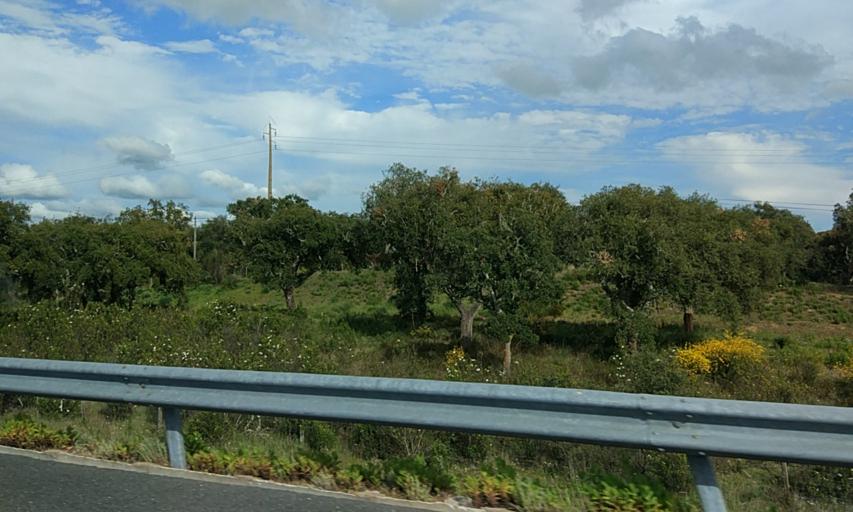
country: PT
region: Evora
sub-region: Evora
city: Evora
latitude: 38.6794
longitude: -7.8223
